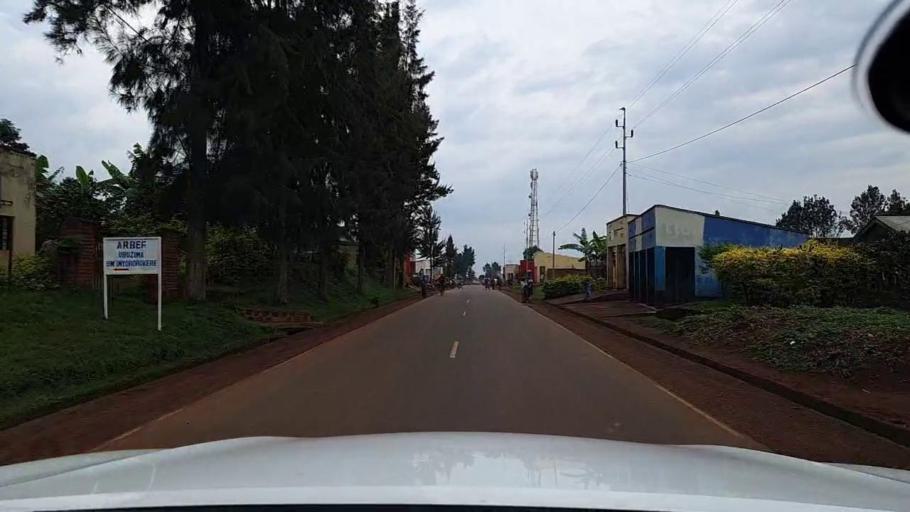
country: RW
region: Western Province
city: Cyangugu
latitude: -2.6254
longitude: 28.9491
